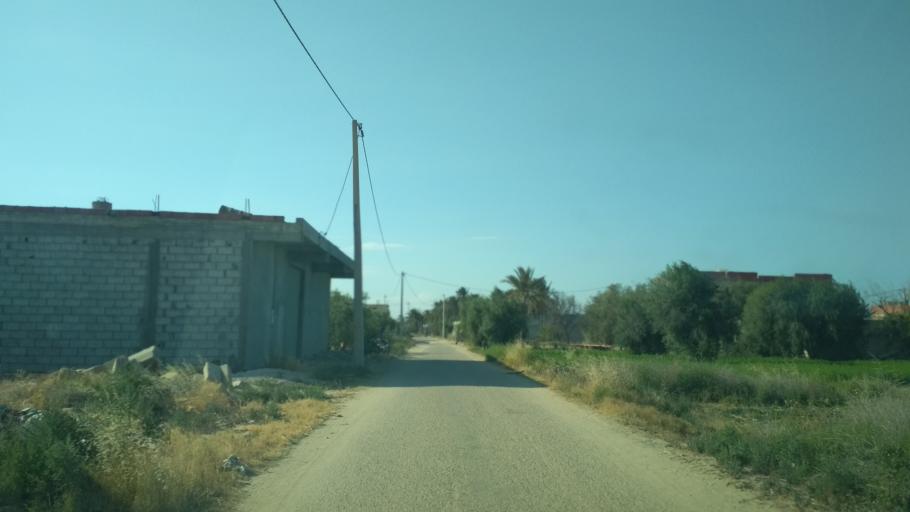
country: TN
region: Qabis
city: Gabes
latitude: 33.9540
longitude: 10.0597
